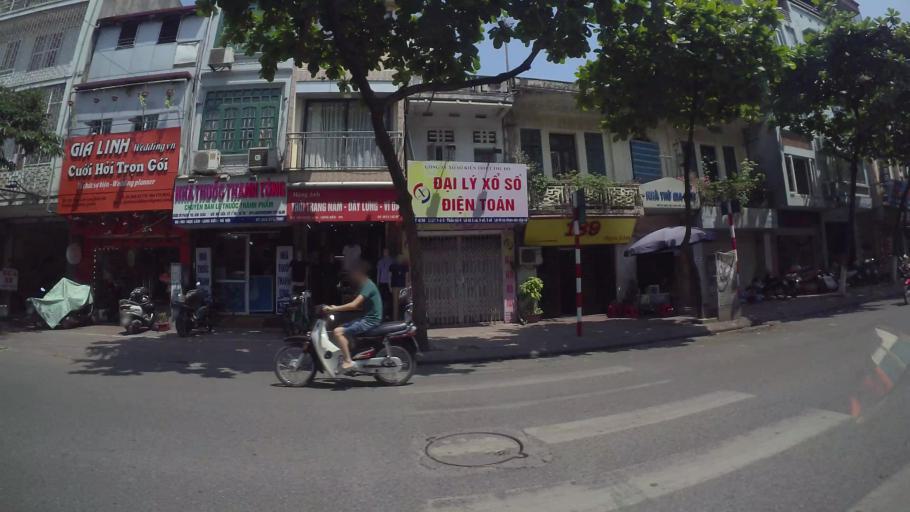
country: VN
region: Ha Noi
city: Hoan Kiem
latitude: 21.0456
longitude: 105.8704
